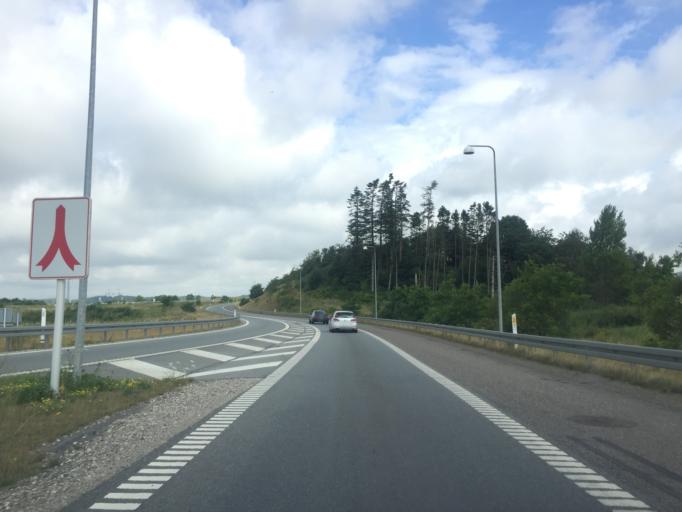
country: DK
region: South Denmark
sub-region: Svendborg Kommune
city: Svendborg
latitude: 55.0728
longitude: 10.5797
